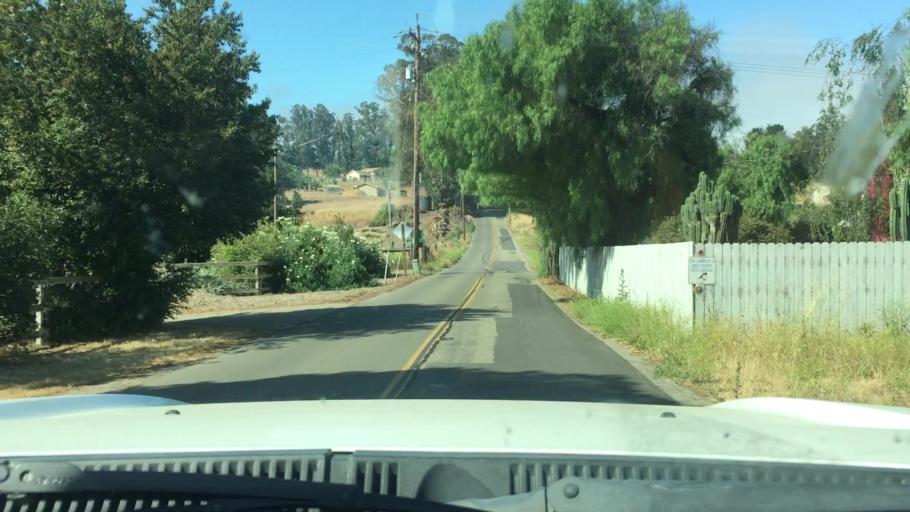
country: US
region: California
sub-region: San Luis Obispo County
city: Callender
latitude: 35.0784
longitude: -120.5485
